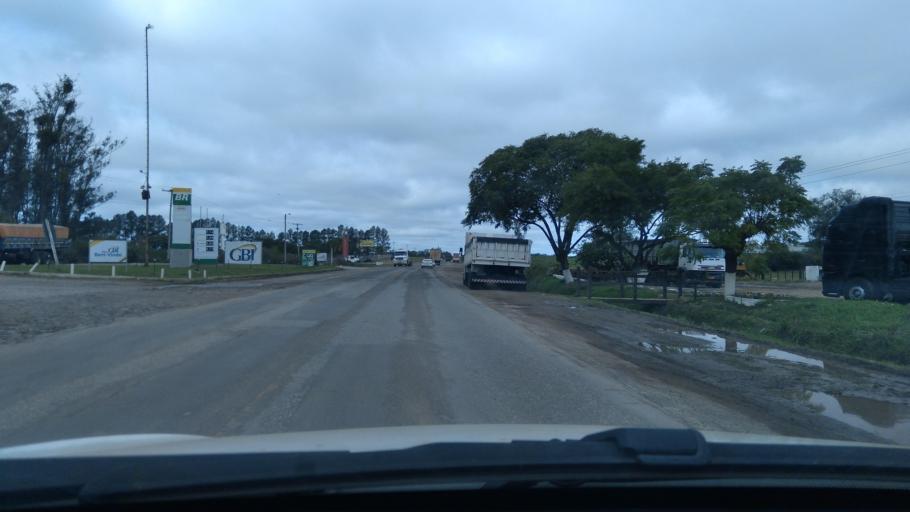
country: BR
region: Rio Grande do Sul
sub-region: Dom Pedrito
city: Dom Pedrito
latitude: -30.9761
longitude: -54.6472
